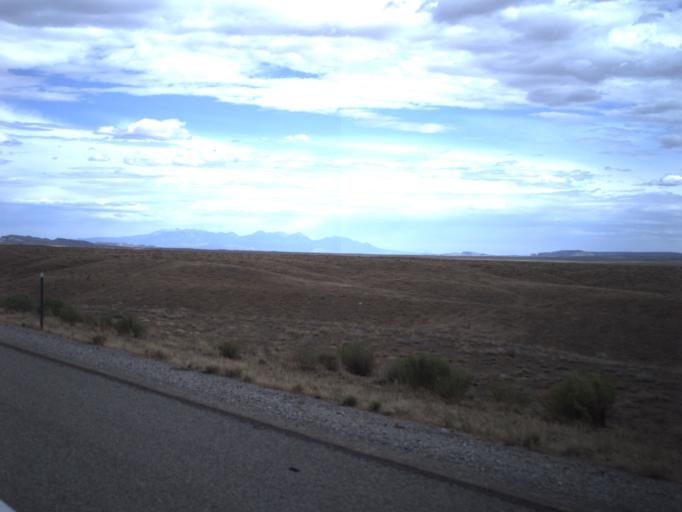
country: US
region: Utah
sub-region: Grand County
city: Moab
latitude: 38.9218
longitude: -109.9636
